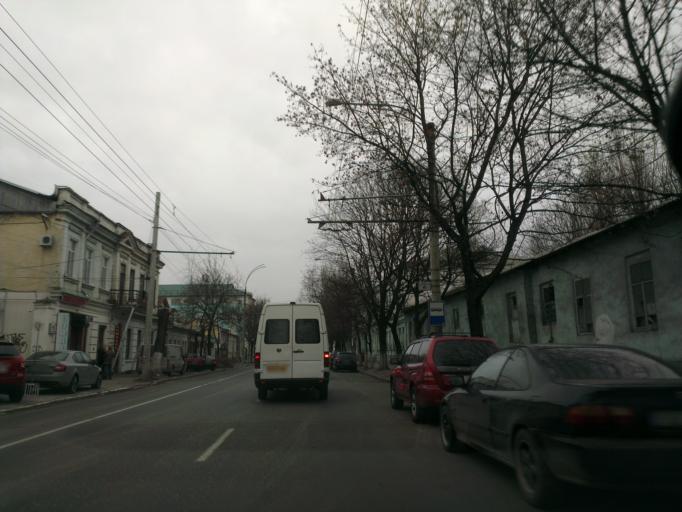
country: MD
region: Chisinau
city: Chisinau
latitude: 47.0146
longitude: 28.8387
